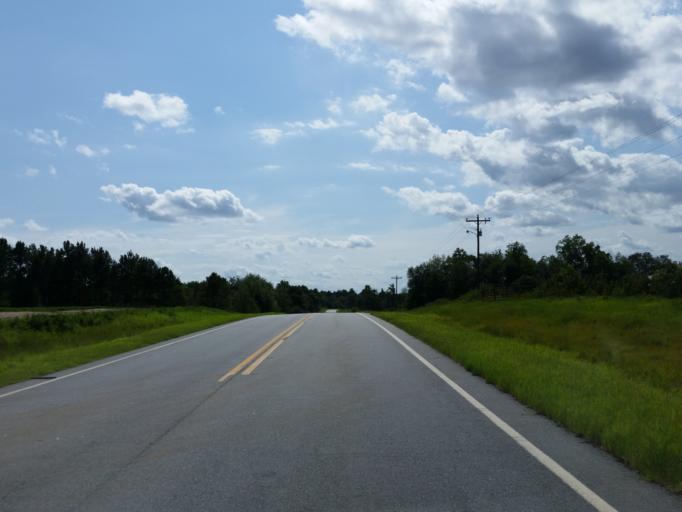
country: US
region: Georgia
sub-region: Turner County
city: Ashburn
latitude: 31.6351
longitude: -83.5056
